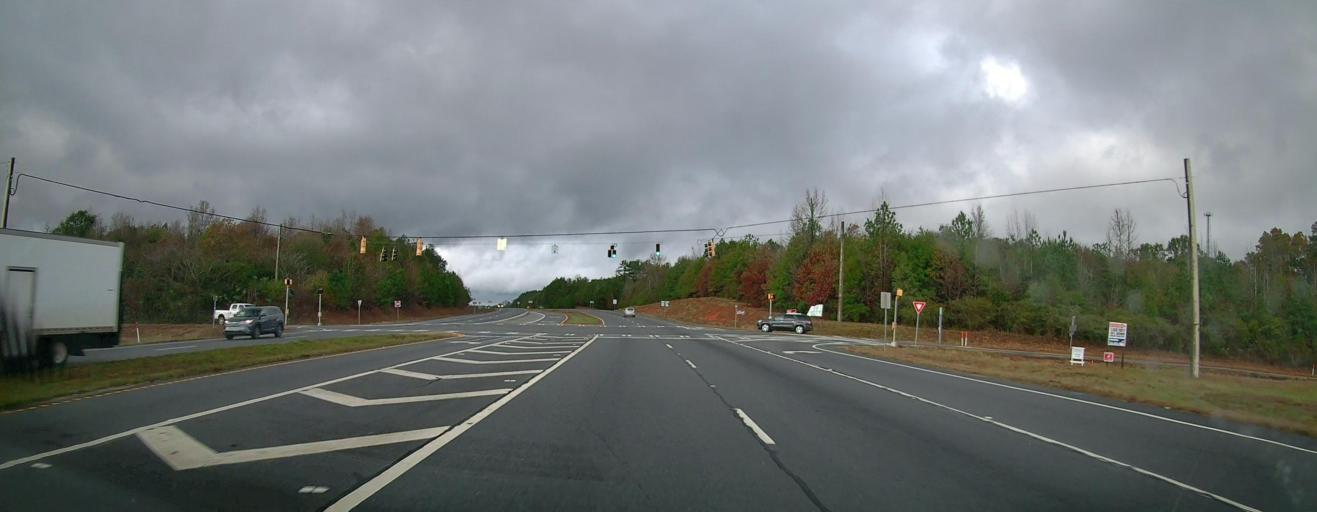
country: US
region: Georgia
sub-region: Clarke County
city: Country Club Estates
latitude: 34.0491
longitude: -83.4060
